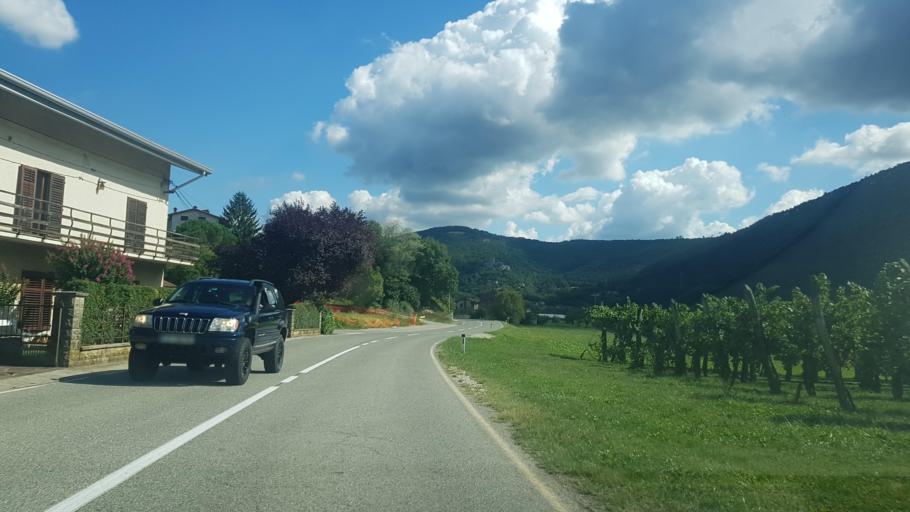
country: SI
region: Komen
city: Komen
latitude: 45.8665
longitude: 13.7801
